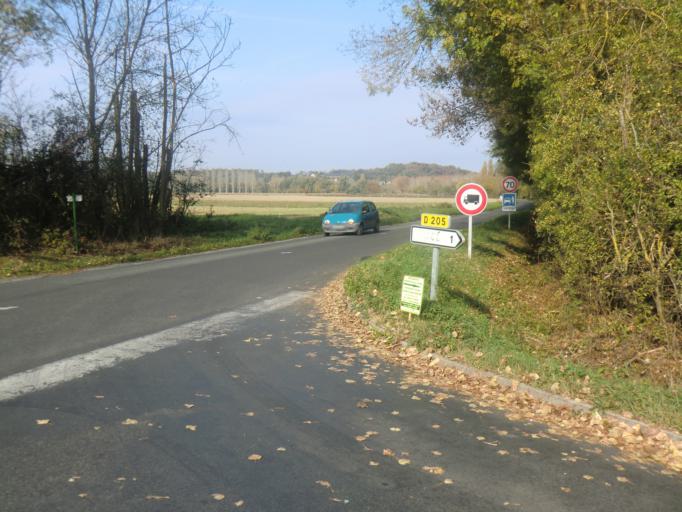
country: FR
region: Pays de la Loire
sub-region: Departement de Maine-et-Loire
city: Chace
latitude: 47.2150
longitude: -0.0908
